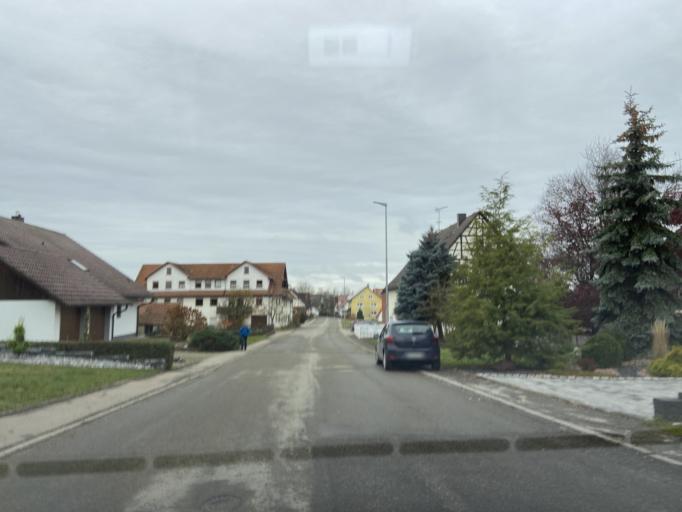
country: DE
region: Baden-Wuerttemberg
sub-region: Tuebingen Region
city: Wald
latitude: 47.9650
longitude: 9.1818
